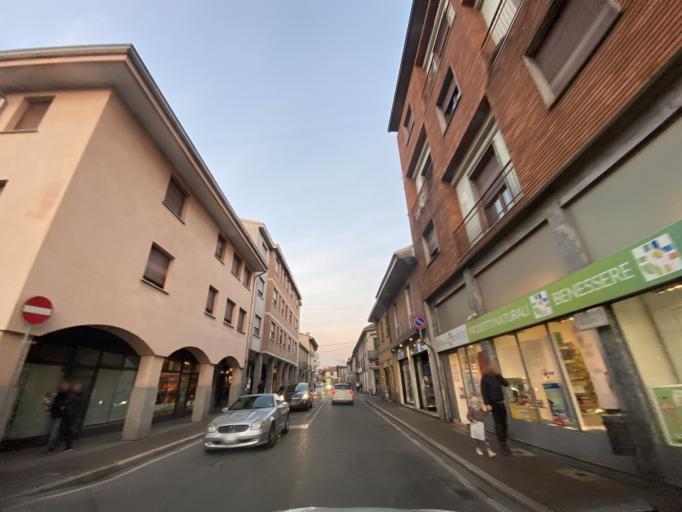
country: IT
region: Lombardy
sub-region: Provincia di Monza e Brianza
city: Varedo
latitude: 45.5970
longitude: 9.1529
